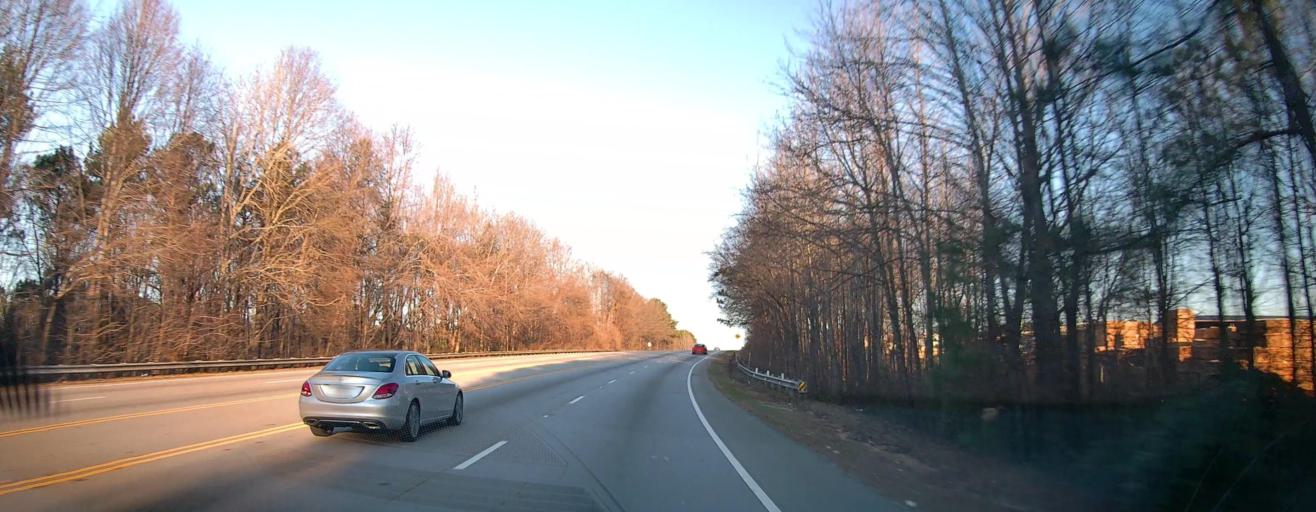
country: US
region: Georgia
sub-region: Fulton County
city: Union City
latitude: 33.5701
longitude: -84.5533
